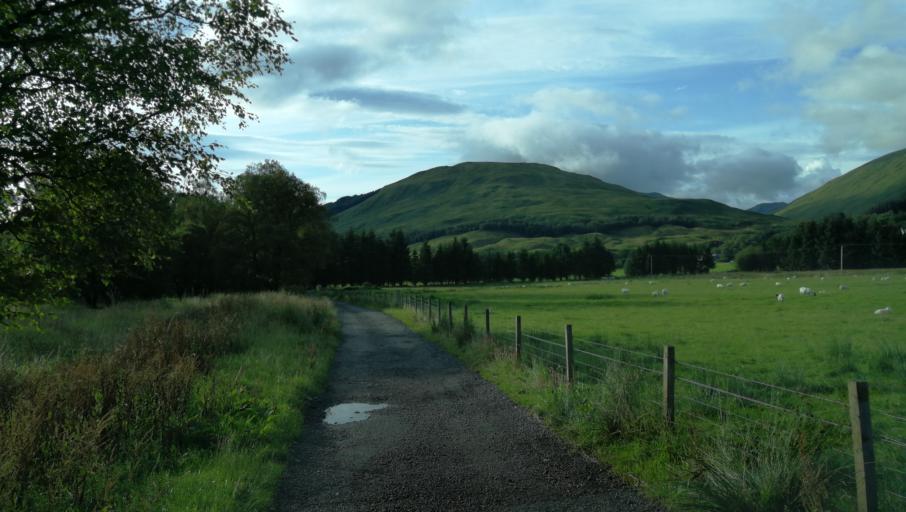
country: GB
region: Scotland
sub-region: Argyll and Bute
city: Garelochhead
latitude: 56.4183
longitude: -4.6682
